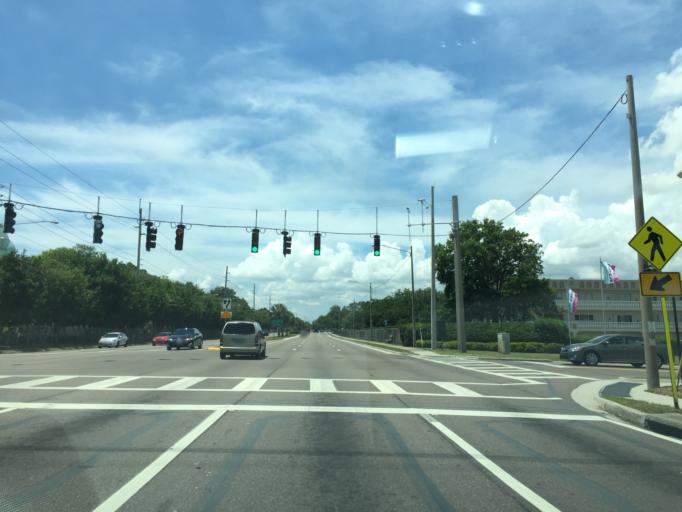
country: US
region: Florida
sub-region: Pinellas County
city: Dunedin
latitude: 28.0001
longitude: -82.7423
